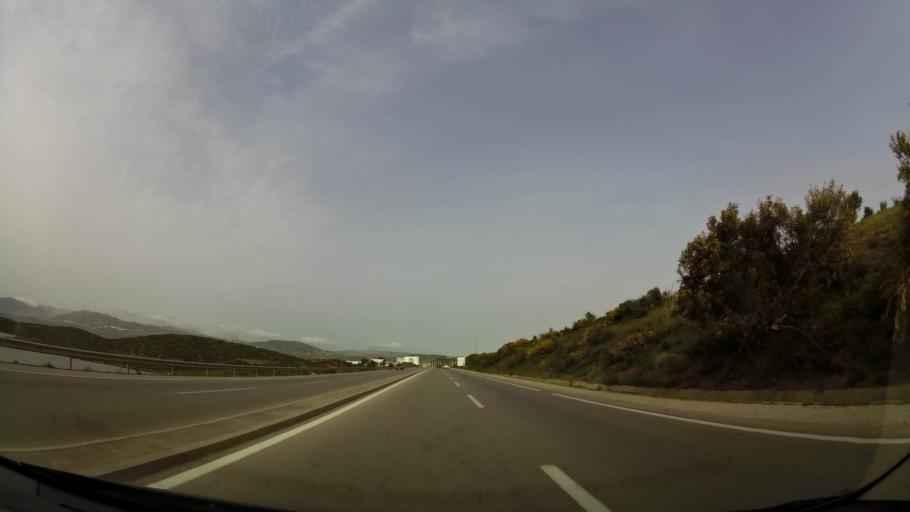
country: MA
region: Tanger-Tetouan
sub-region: Tetouan
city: Saddina
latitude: 35.5629
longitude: -5.4925
